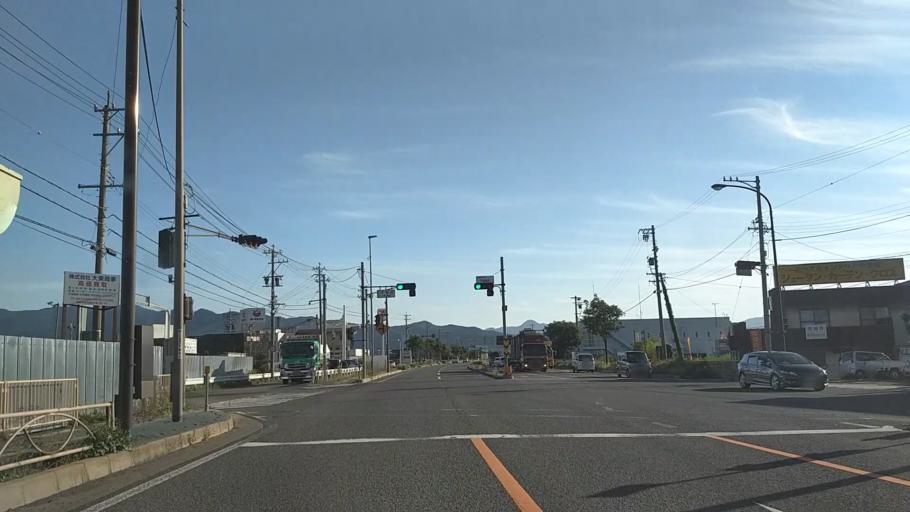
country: JP
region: Nagano
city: Nagano-shi
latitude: 36.6021
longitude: 138.1942
